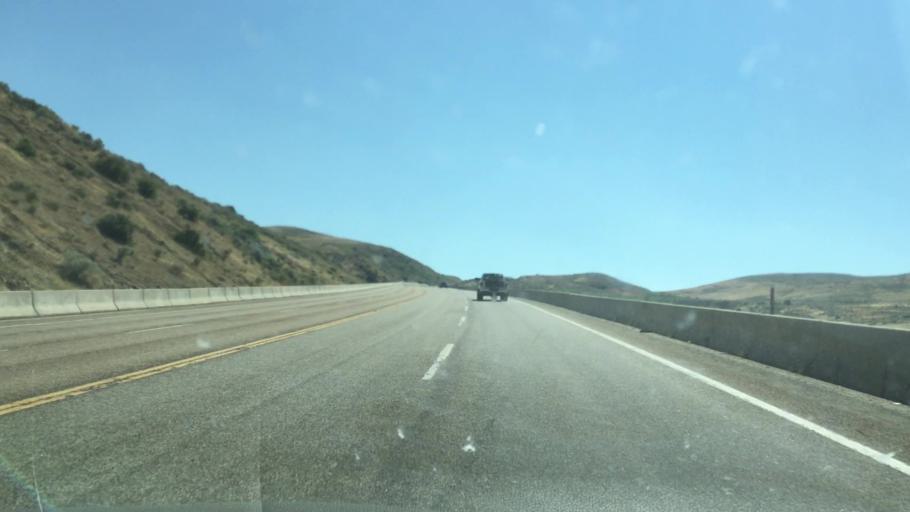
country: US
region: Idaho
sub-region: Ada County
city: Eagle
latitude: 43.8439
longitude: -116.2332
